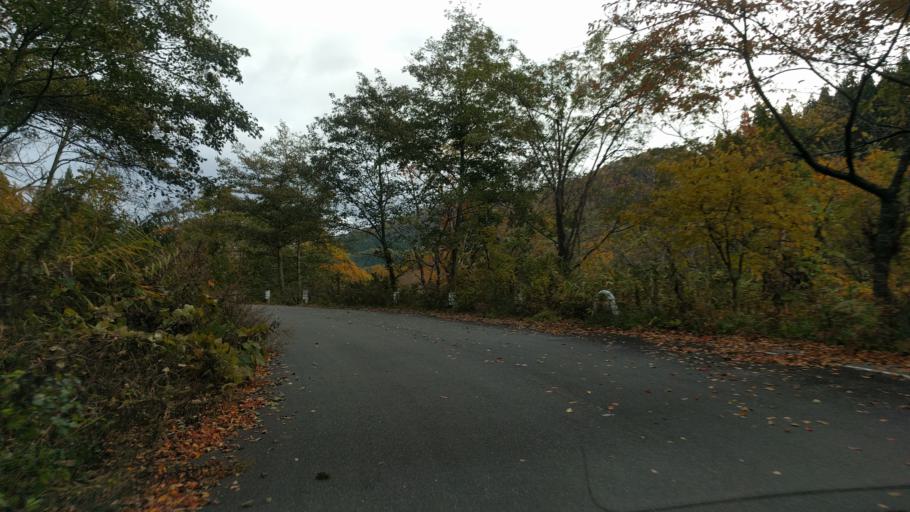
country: JP
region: Fukushima
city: Kitakata
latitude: 37.3912
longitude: 139.7377
